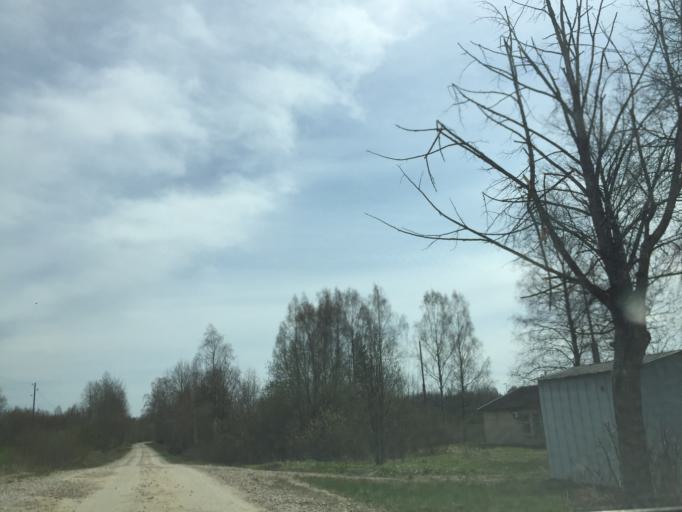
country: LV
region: Ludzas Rajons
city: Ludza
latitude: 56.5343
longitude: 27.5341
